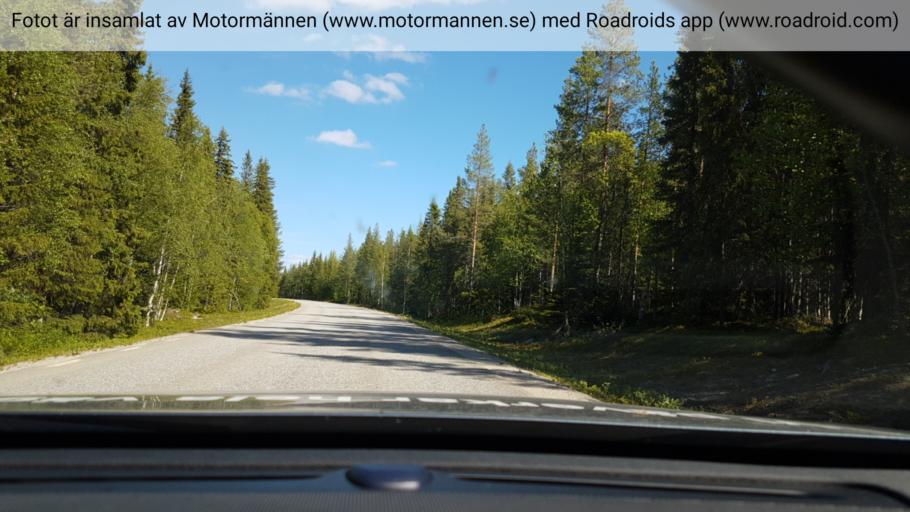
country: SE
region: Vaesterbotten
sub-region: Lycksele Kommun
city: Soderfors
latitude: 64.6323
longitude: 17.9852
